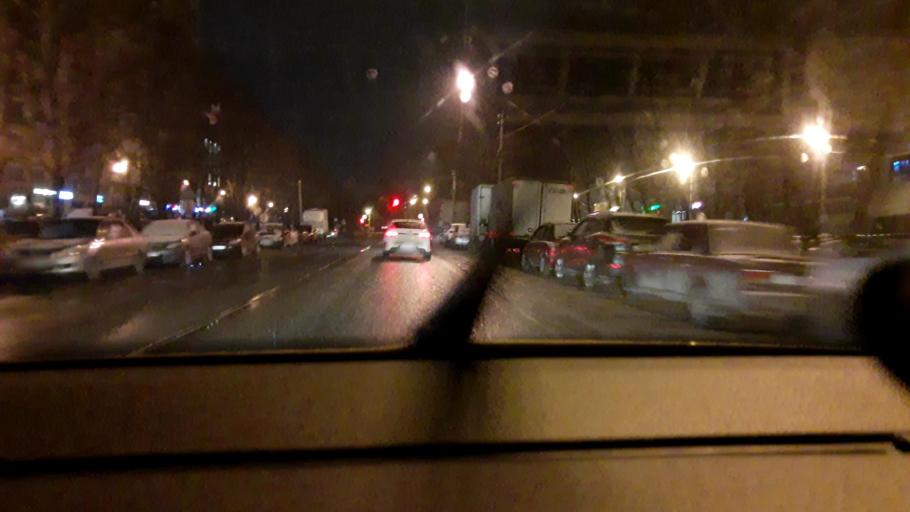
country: RU
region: Moskovskaya
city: Shchelkovo
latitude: 55.9377
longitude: 37.9746
